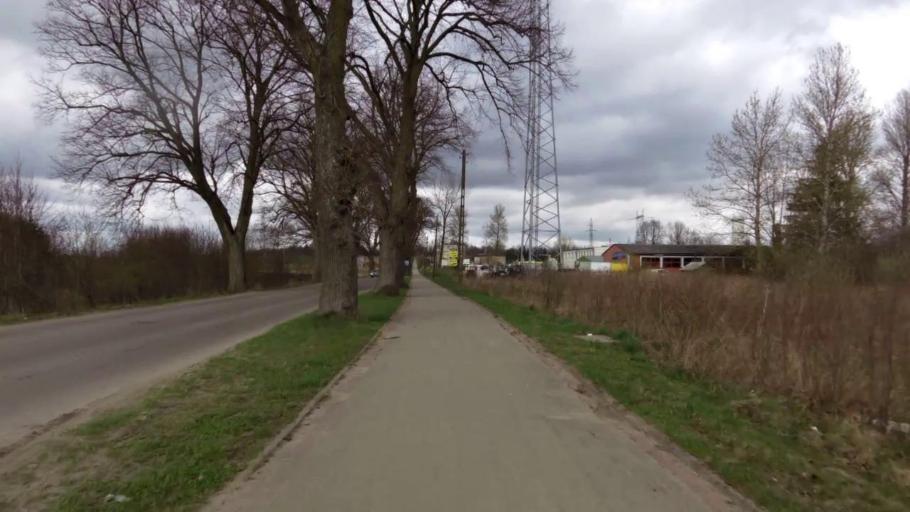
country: PL
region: West Pomeranian Voivodeship
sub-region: Powiat koszalinski
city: Sianow
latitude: 54.2360
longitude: 16.2991
